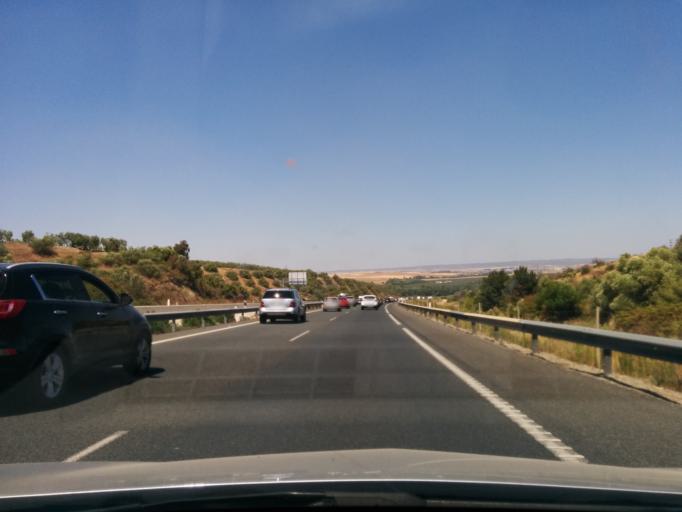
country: ES
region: Andalusia
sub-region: Provincia de Sevilla
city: Benacazon
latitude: 37.3648
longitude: -6.2117
